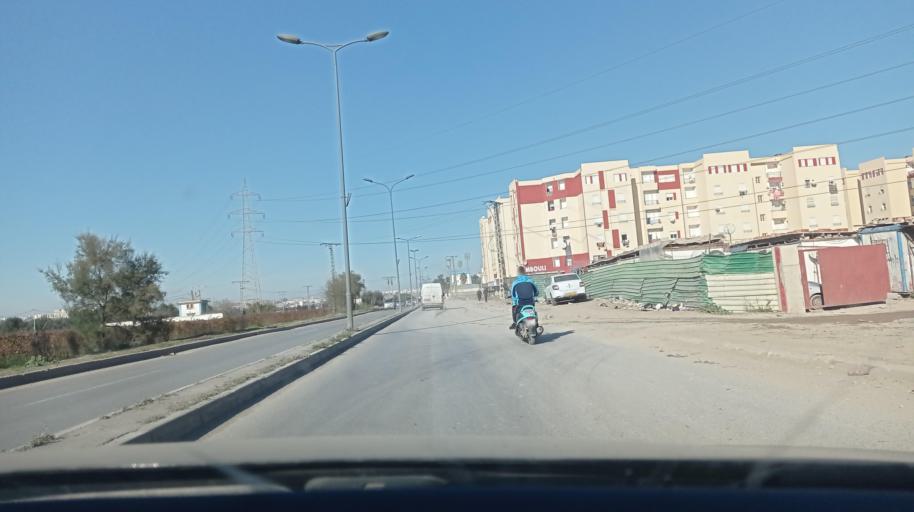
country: DZ
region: Tipaza
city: Baraki
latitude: 36.6627
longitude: 3.0855
